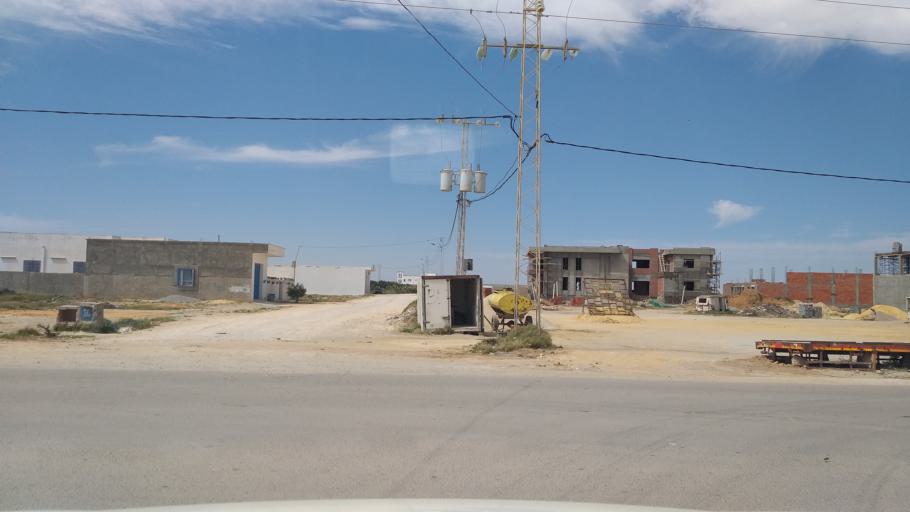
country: TN
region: Al Mahdiyah
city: El Jem
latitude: 35.3055
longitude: 10.6920
